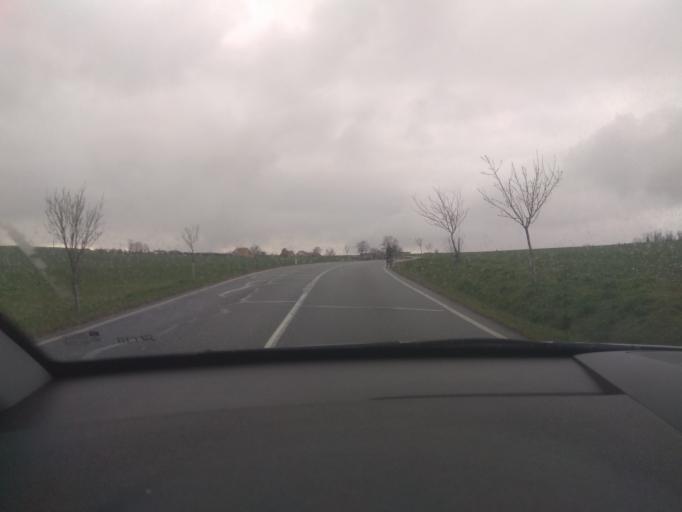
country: CZ
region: South Moravian
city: Zastavka
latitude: 49.1796
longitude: 16.3601
